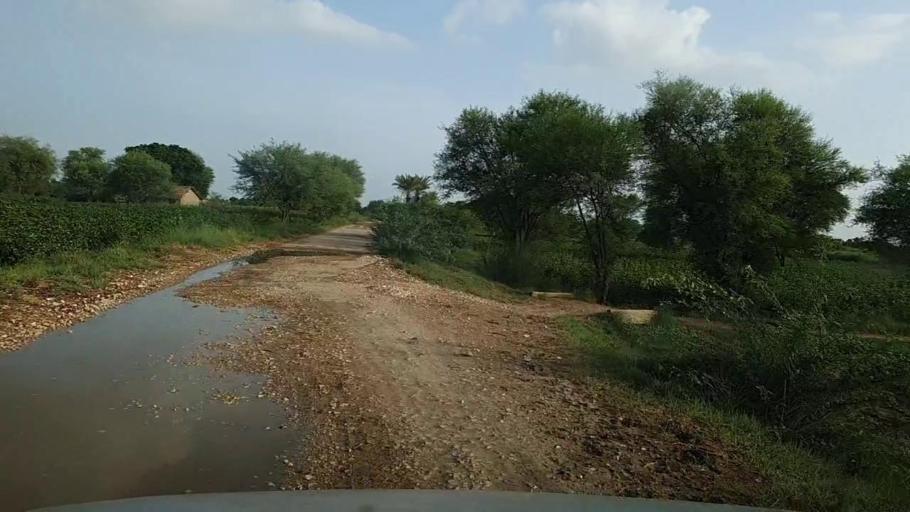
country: PK
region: Sindh
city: Pad Idan
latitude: 26.7859
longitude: 68.2204
